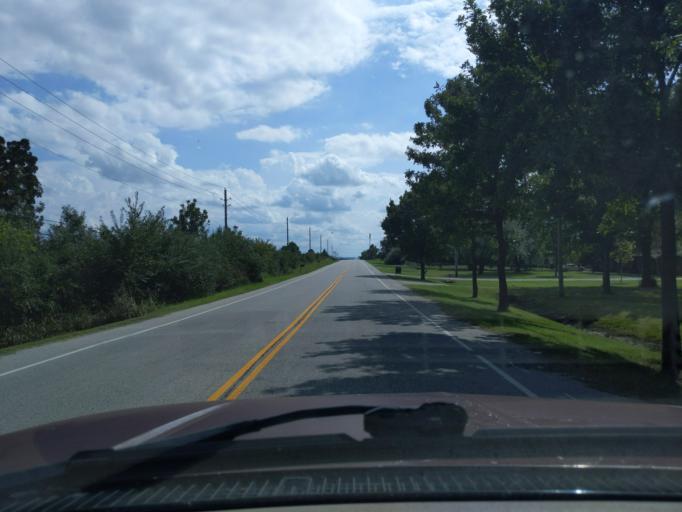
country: US
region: Oklahoma
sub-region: Tulsa County
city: Jenks
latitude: 36.0506
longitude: -96.0116
